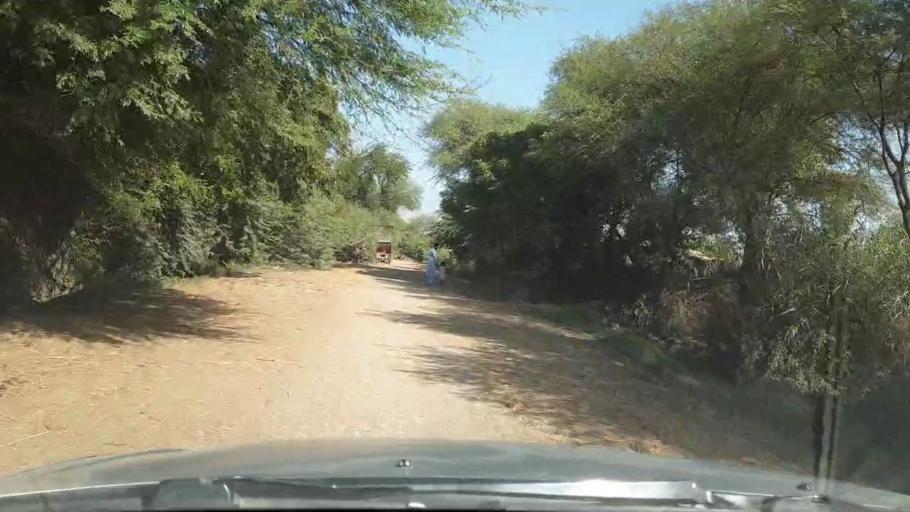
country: PK
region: Sindh
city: Matli
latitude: 24.9476
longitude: 68.5369
